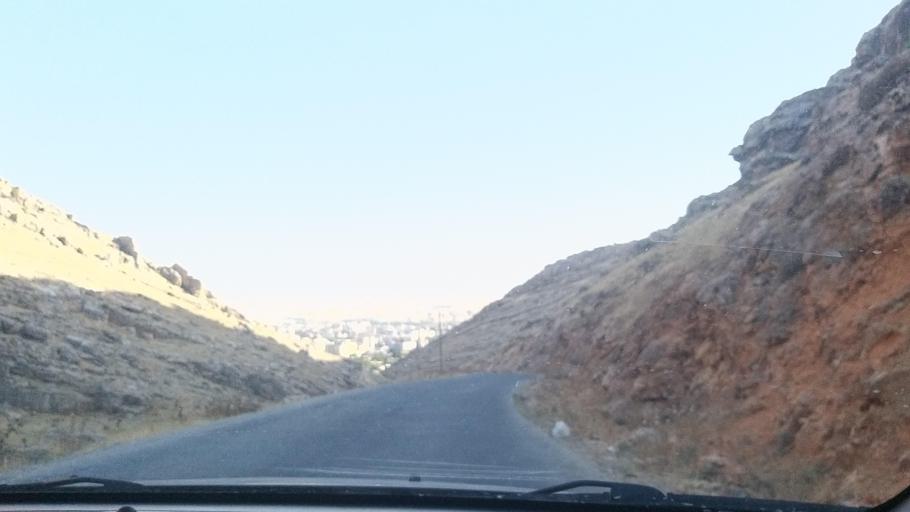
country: TR
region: Diyarbakir
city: Silvan
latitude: 38.1598
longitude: 41.0030
